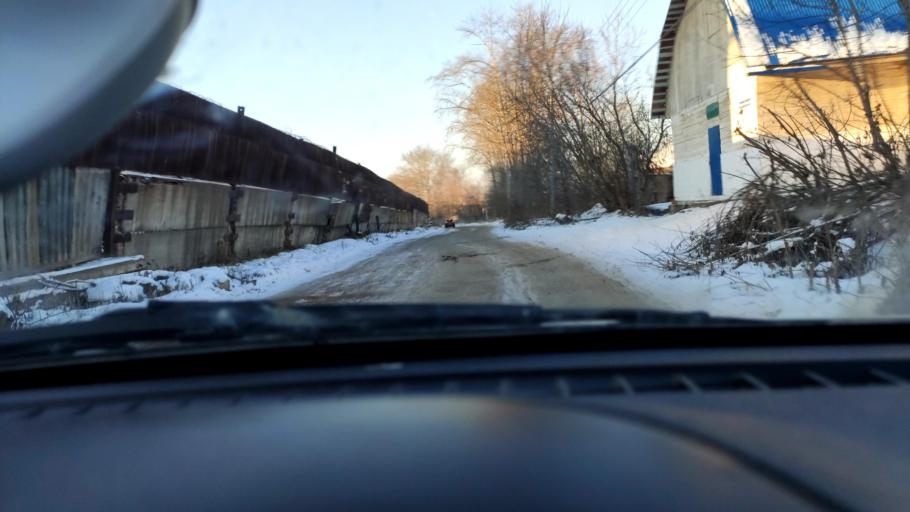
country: RU
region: Perm
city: Perm
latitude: 58.0718
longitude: 56.3584
